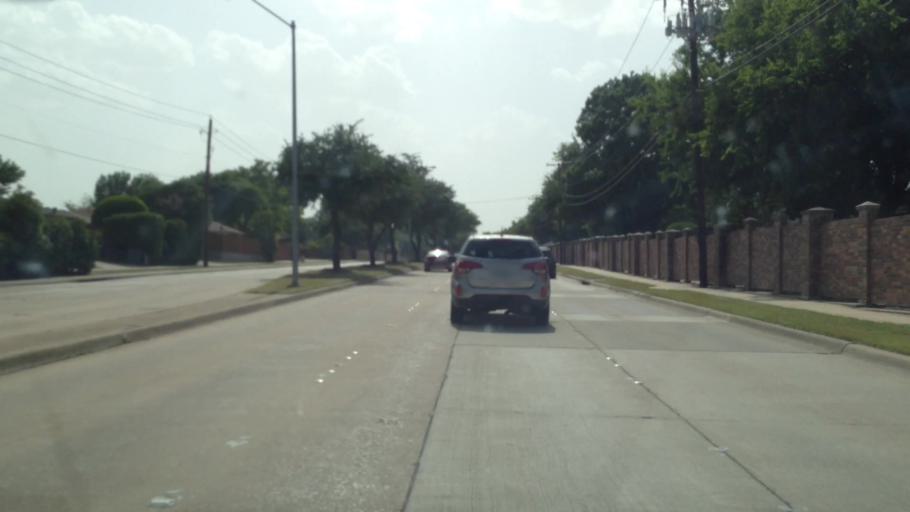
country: US
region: Texas
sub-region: Collin County
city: Plano
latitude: 33.0266
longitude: -96.7374
